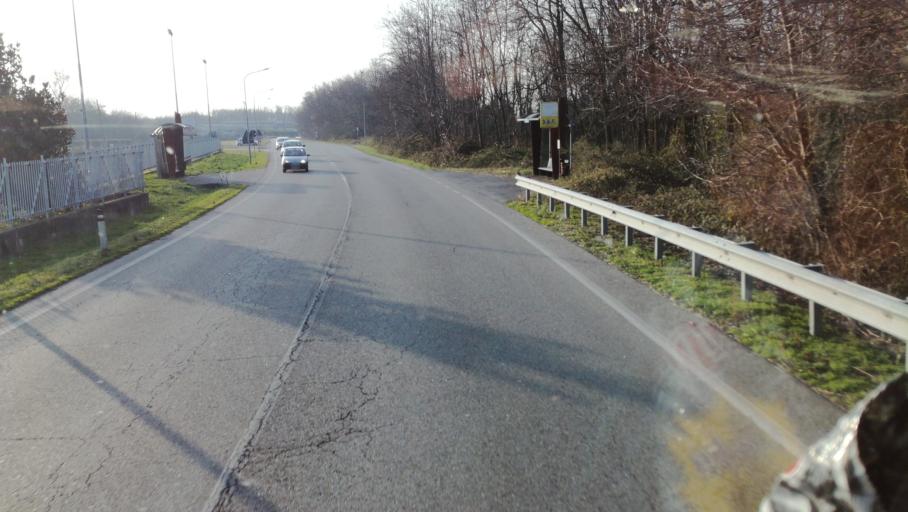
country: IT
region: Piedmont
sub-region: Provincia di Novara
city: Vaprio D'Agogna
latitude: 45.5991
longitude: 8.5339
